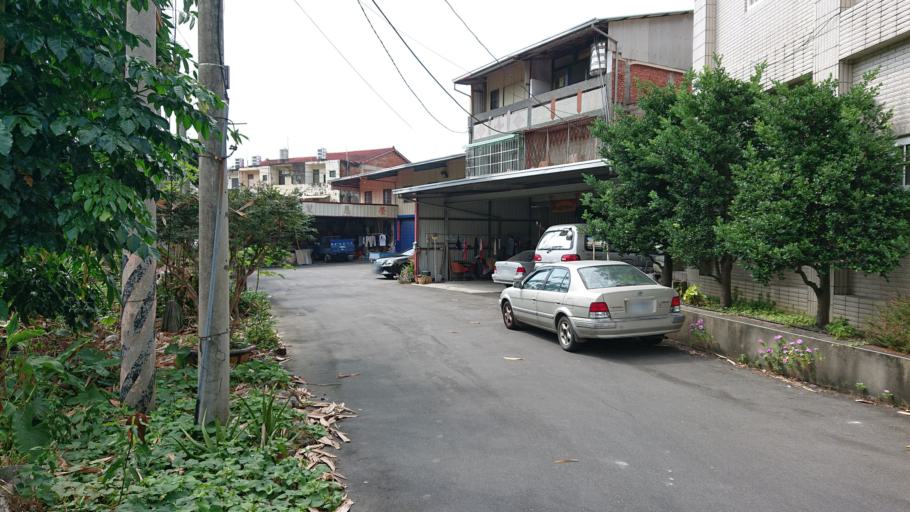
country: TW
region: Taiwan
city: Lugu
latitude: 23.7595
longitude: 120.7049
